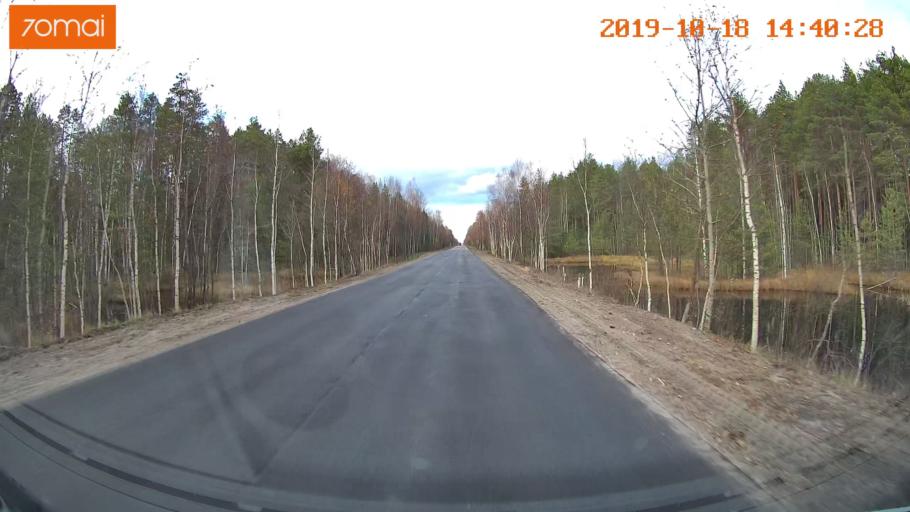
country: RU
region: Vladimir
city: Velikodvorskiy
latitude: 55.2770
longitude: 40.6690
